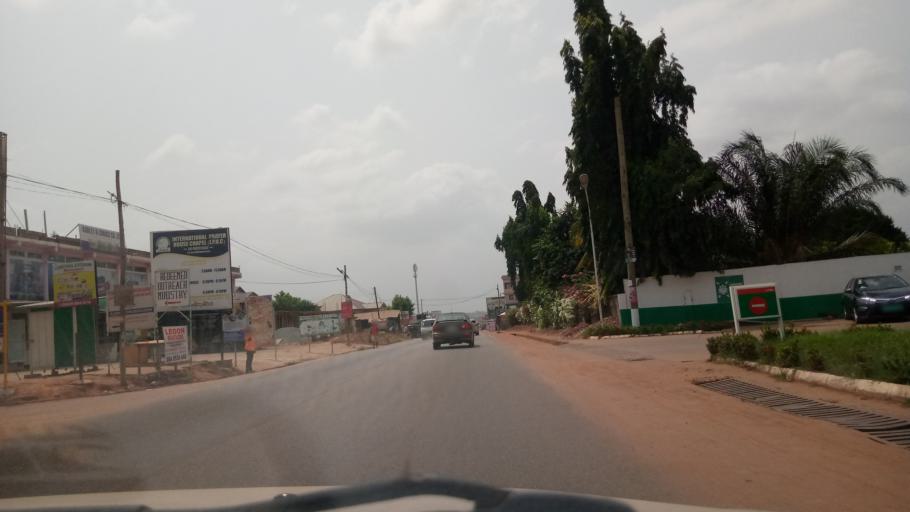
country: GH
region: Greater Accra
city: Medina Estates
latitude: 5.6845
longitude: -0.1937
